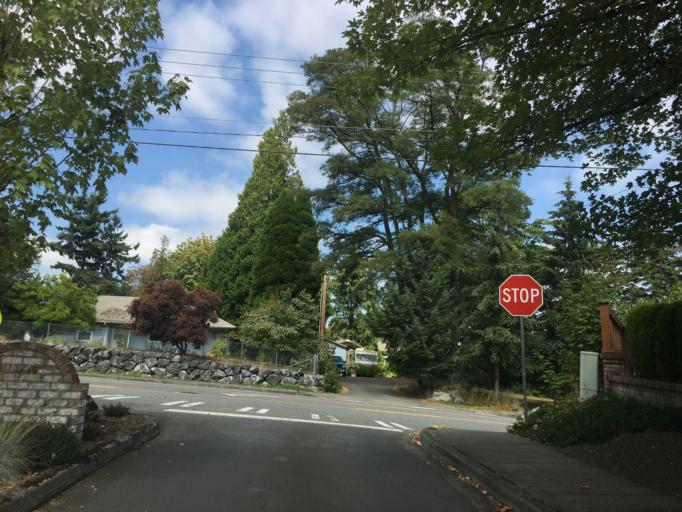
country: US
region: Washington
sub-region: King County
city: Woodinville
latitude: 47.7486
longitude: -122.1812
